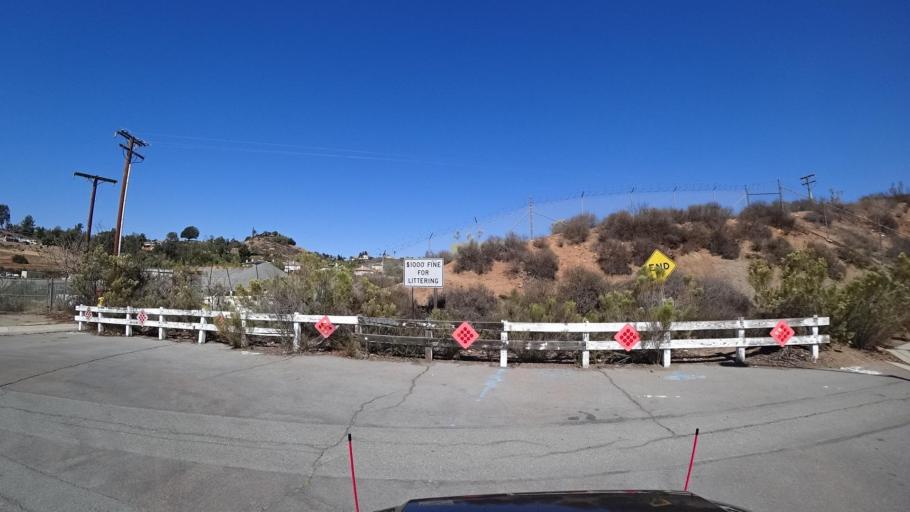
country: US
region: California
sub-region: San Diego County
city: Rancho San Diego
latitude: 32.7584
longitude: -116.9350
